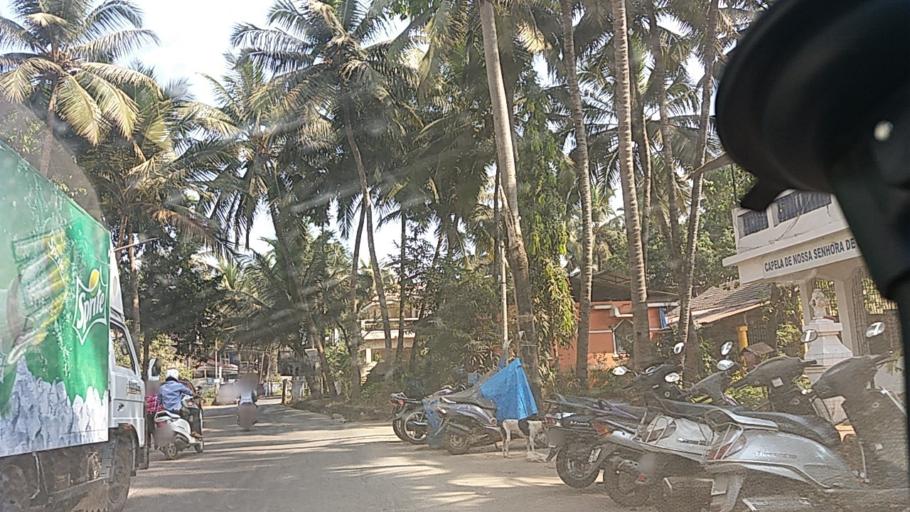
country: IN
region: Goa
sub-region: South Goa
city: Madgaon
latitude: 15.2843
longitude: 73.9538
